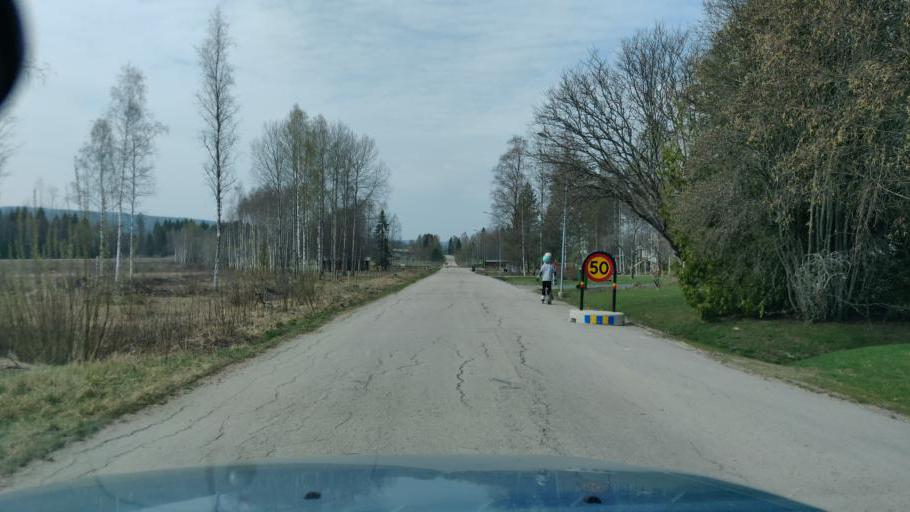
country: SE
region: Vaermland
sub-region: Munkfors Kommun
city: Munkfors
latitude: 59.8366
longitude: 13.5082
